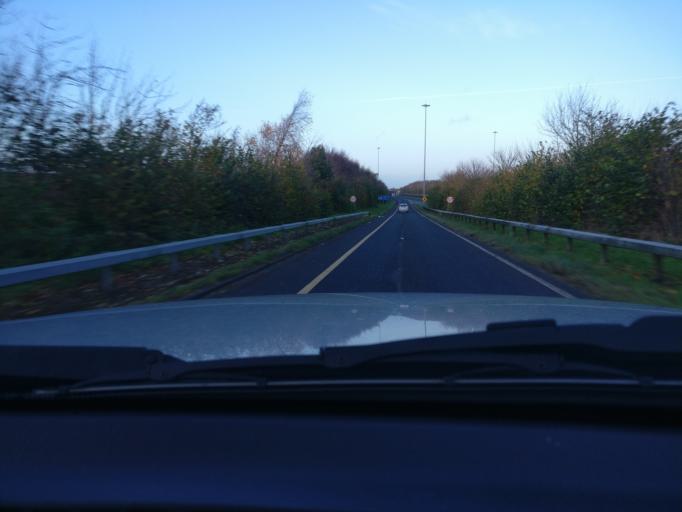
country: IE
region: Leinster
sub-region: Lu
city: Dunleer
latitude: 53.8613
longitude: -6.4288
